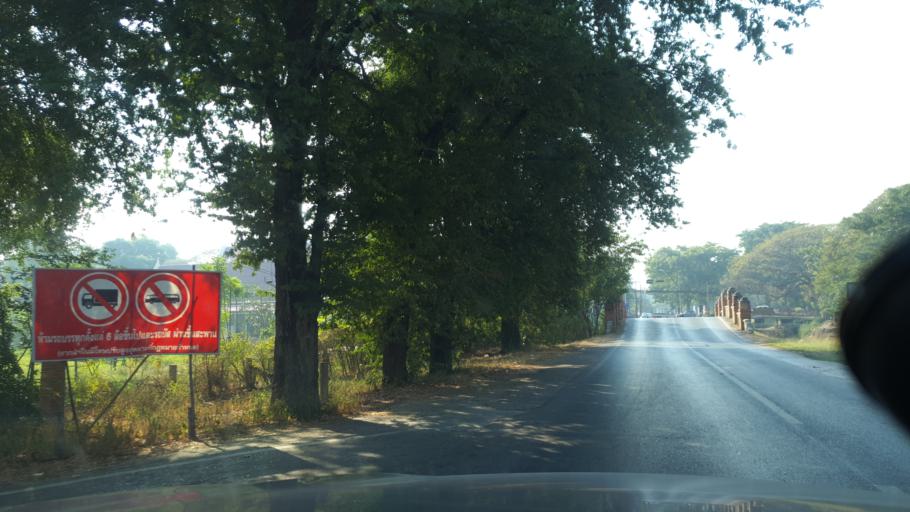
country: TH
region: Phra Nakhon Si Ayutthaya
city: Phra Nakhon Si Ayutthaya
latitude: 14.3530
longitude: 100.5560
